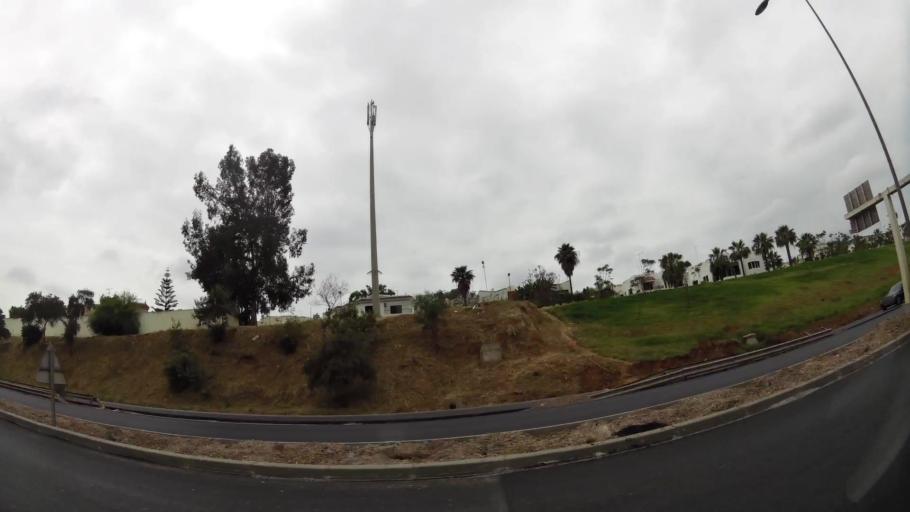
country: MA
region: Rabat-Sale-Zemmour-Zaer
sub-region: Rabat
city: Rabat
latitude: 33.9668
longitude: -6.8196
